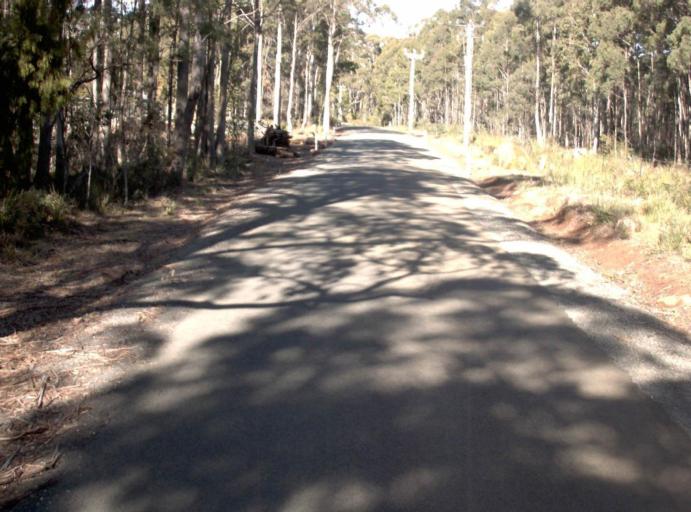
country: AU
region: Tasmania
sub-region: Launceston
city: Mayfield
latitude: -41.3173
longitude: 147.2079
